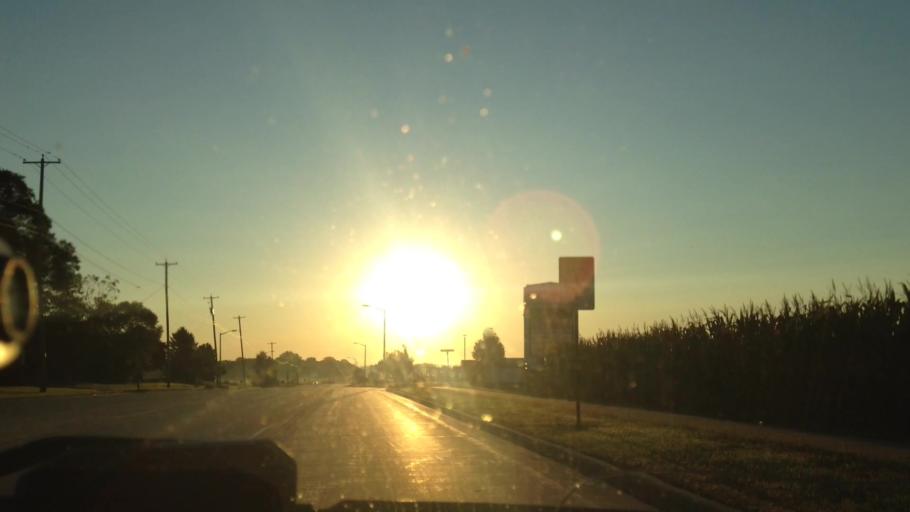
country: US
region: Wisconsin
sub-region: Washington County
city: West Bend
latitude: 43.4266
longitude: -88.1476
